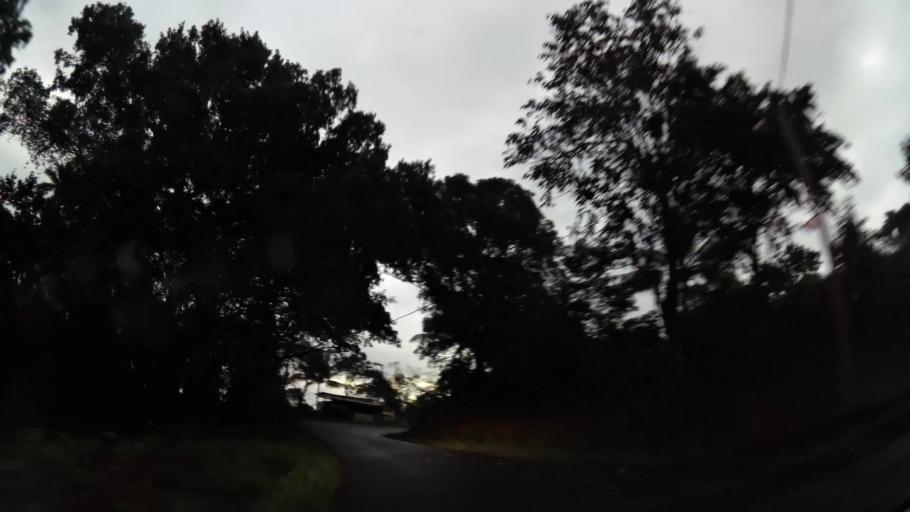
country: DM
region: Saint Andrew
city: Wesley
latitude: 15.5854
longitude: -61.3241
